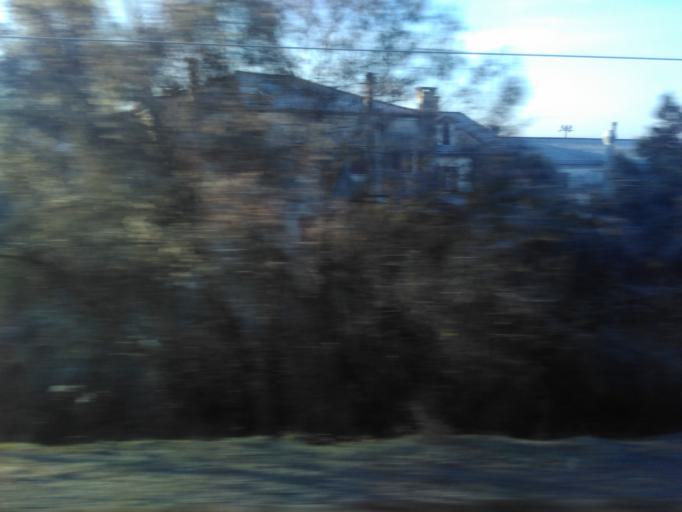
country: IT
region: Veneto
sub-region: Provincia di Padova
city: Campodoro
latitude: 45.4707
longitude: 11.7446
